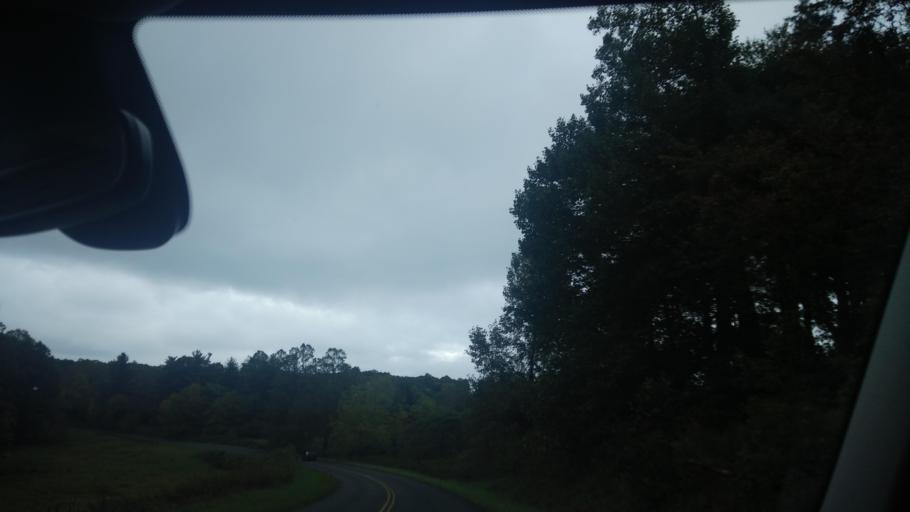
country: US
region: Virginia
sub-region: Carroll County
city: Cana
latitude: 36.6706
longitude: -80.6340
